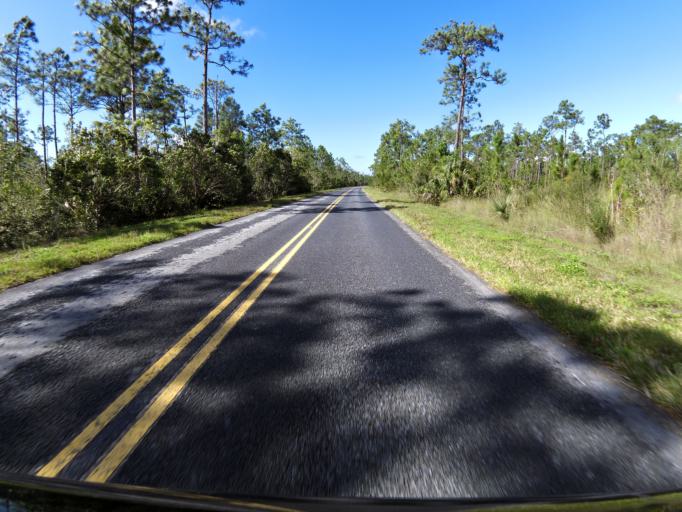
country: US
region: Florida
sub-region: Miami-Dade County
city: Florida City
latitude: 25.4206
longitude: -80.6760
